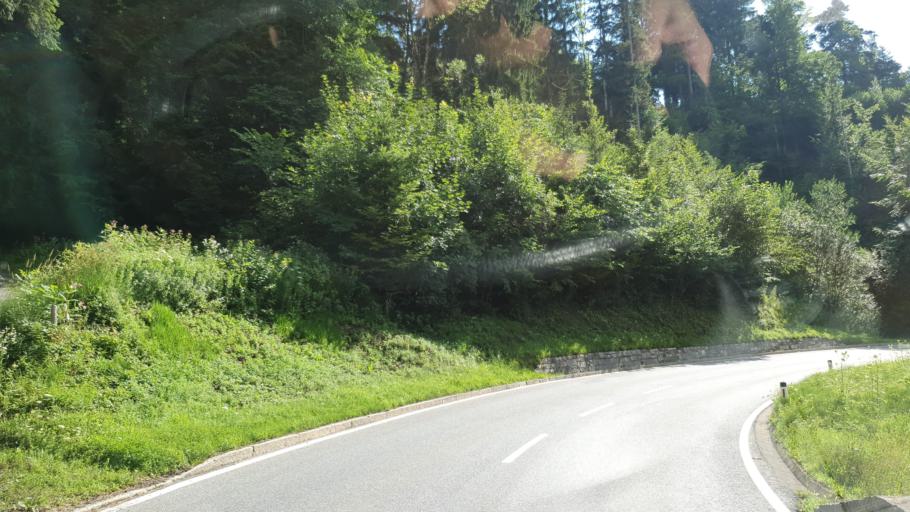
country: AT
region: Vorarlberg
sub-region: Politischer Bezirk Bregenz
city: Kennelbach
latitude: 47.4918
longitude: 9.7775
